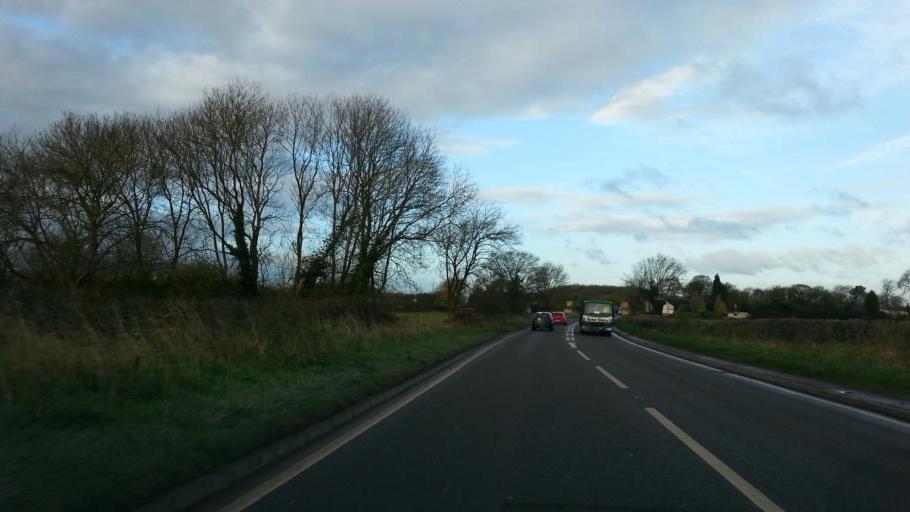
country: GB
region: England
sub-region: Leicestershire
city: Coalville
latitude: 52.7326
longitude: -1.4025
